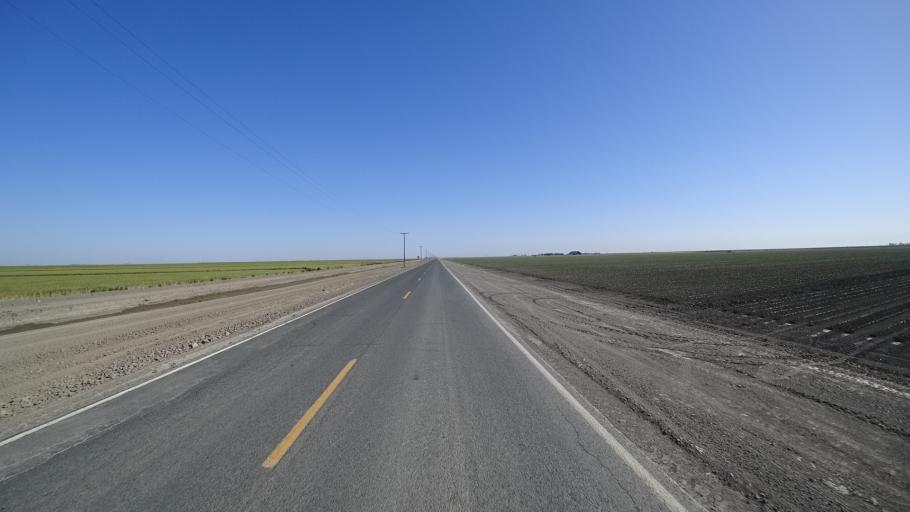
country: US
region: California
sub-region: Kings County
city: Corcoran
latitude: 36.0884
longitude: -119.6440
